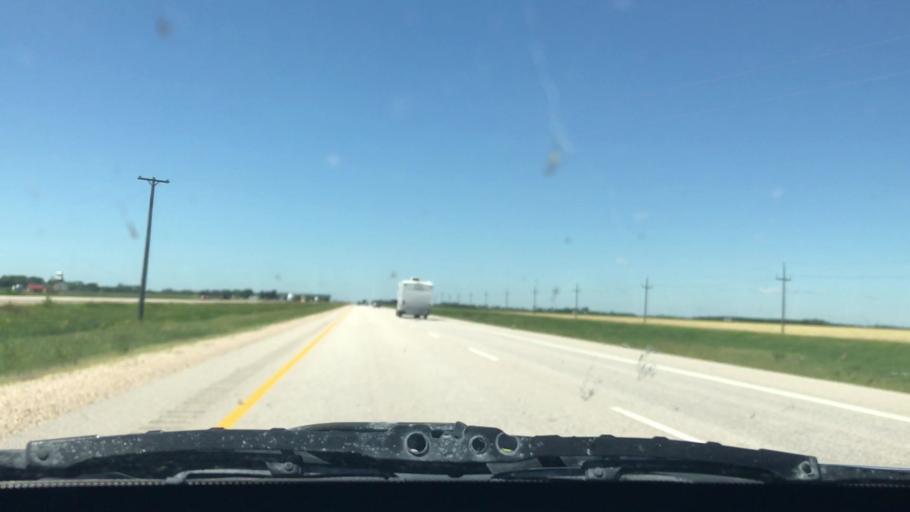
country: CA
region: Manitoba
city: Steinbach
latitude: 49.7228
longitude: -96.7000
